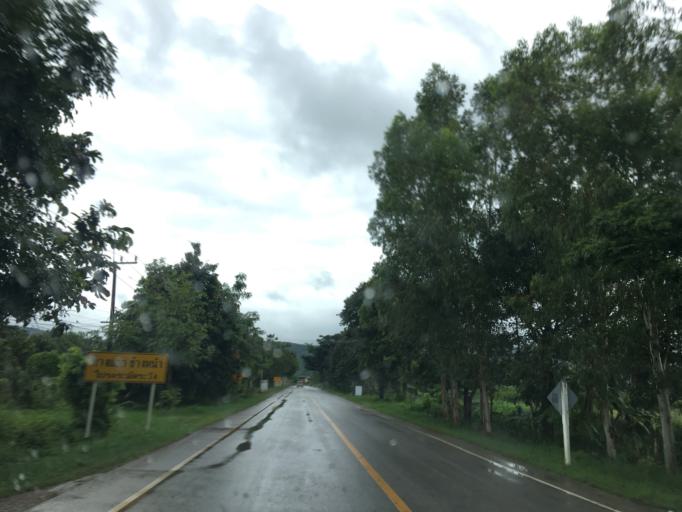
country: TH
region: Chiang Rai
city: Pa Daet
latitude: 19.4965
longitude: 99.9629
